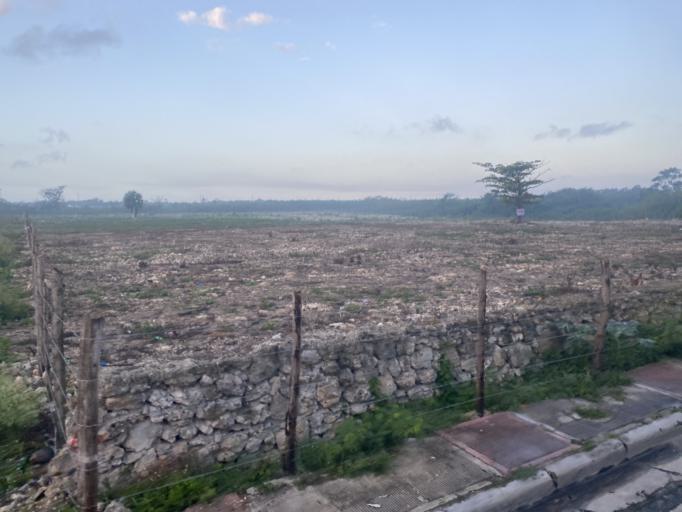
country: DO
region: San Juan
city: Punta Cana
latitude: 18.7107
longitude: -68.4636
